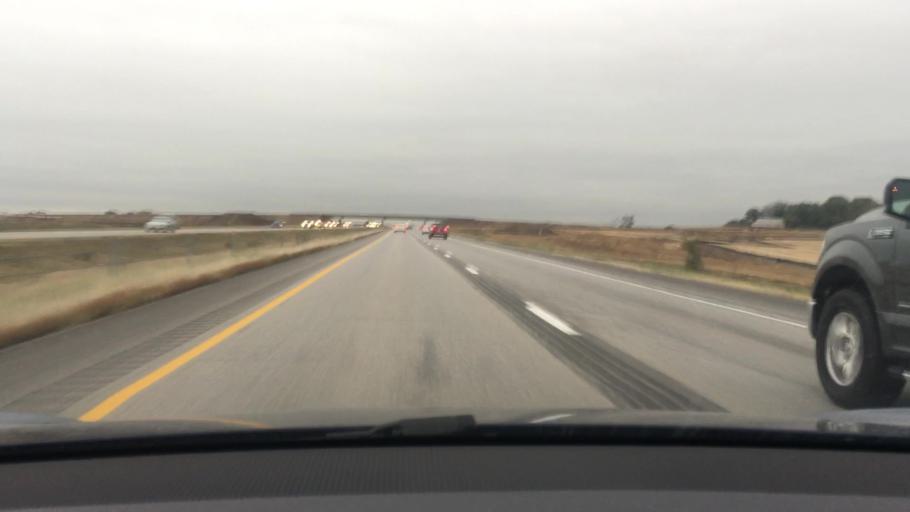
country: US
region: Iowa
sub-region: Johnson County
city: Tiffin
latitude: 41.7284
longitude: -91.6424
